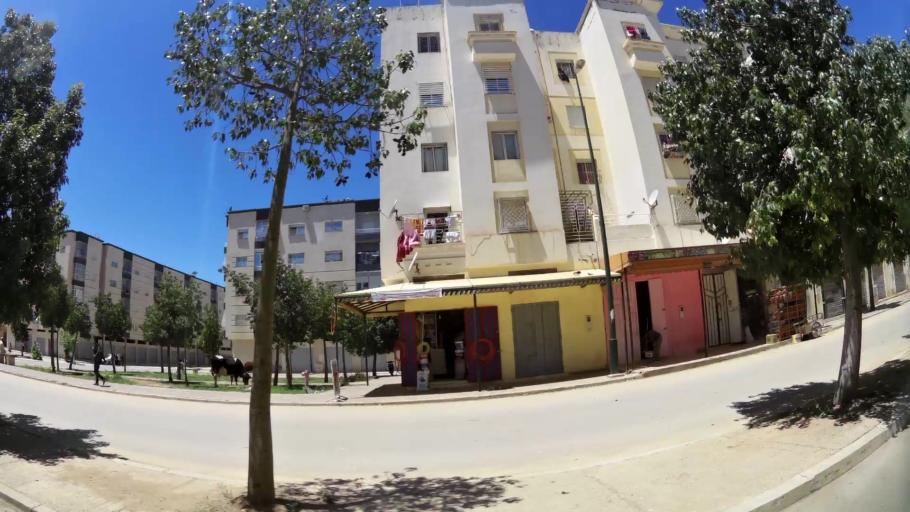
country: MA
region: Meknes-Tafilalet
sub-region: Meknes
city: Meknes
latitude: 33.8630
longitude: -5.5620
